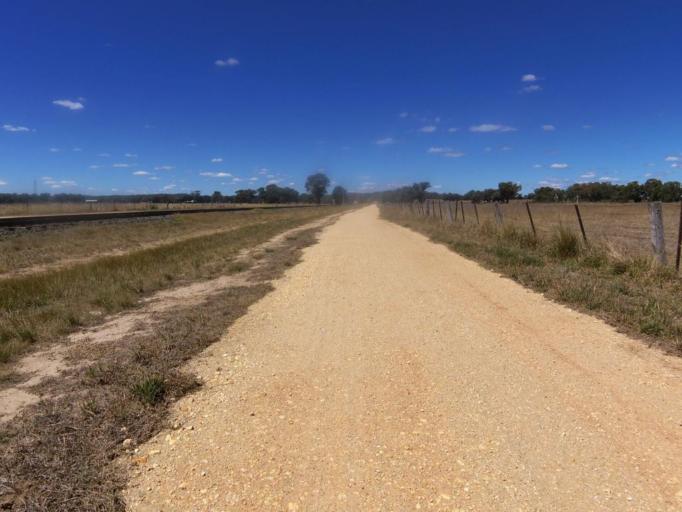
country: AU
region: Victoria
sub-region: Mount Alexander
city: Castlemaine
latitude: -37.0181
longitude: 144.1443
